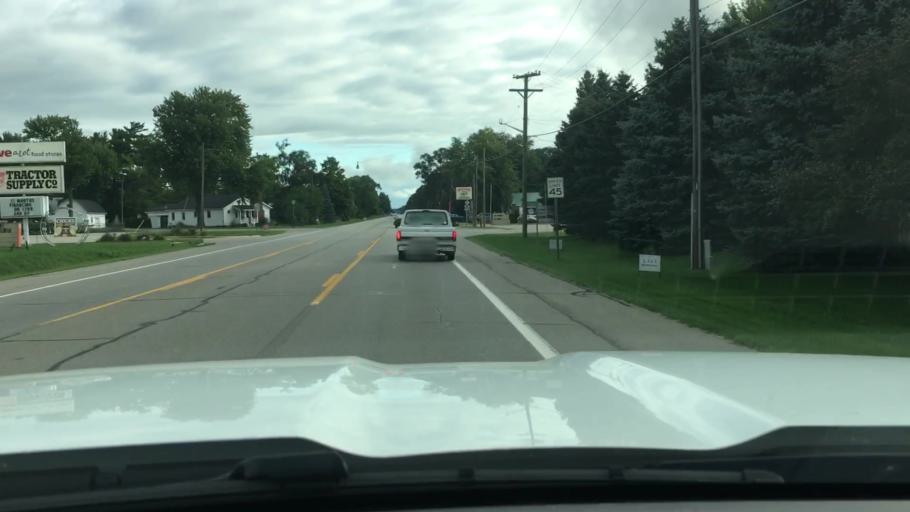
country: US
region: Michigan
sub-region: Tuscola County
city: Caro
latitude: 43.5025
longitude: -83.3785
